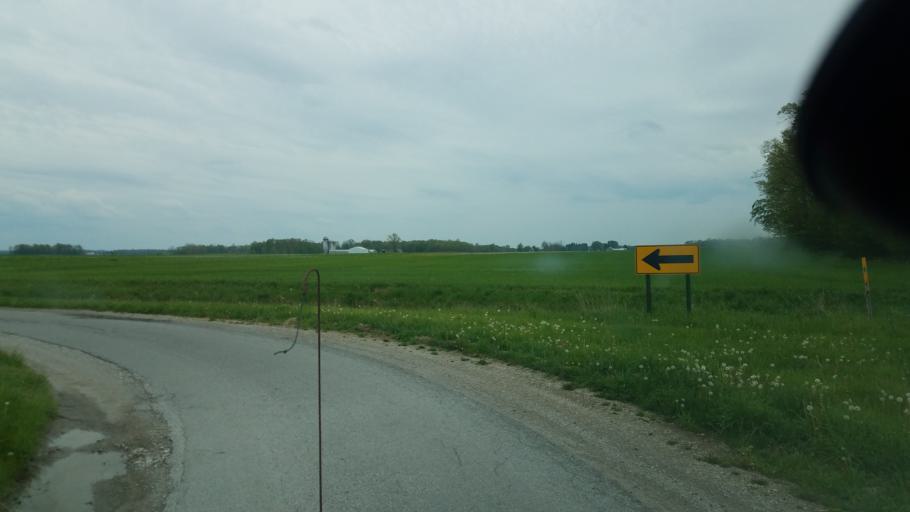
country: US
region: Ohio
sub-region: Huron County
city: Willard
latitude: 41.0049
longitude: -82.7979
